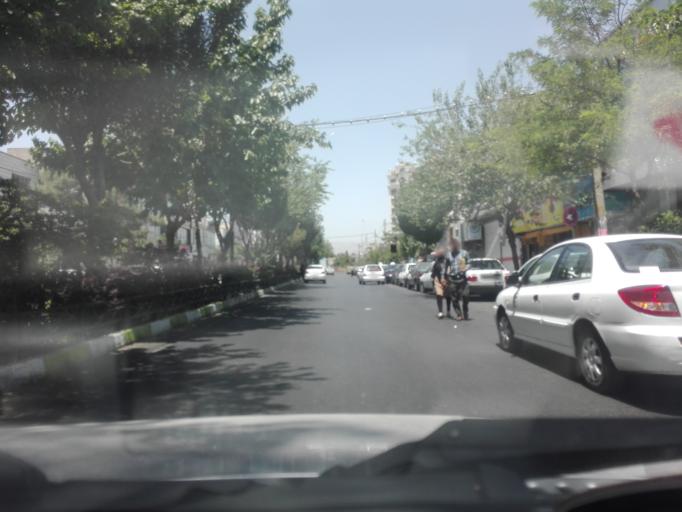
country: IR
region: Tehran
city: Shahre Jadide Andisheh
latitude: 35.7316
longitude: 50.9904
